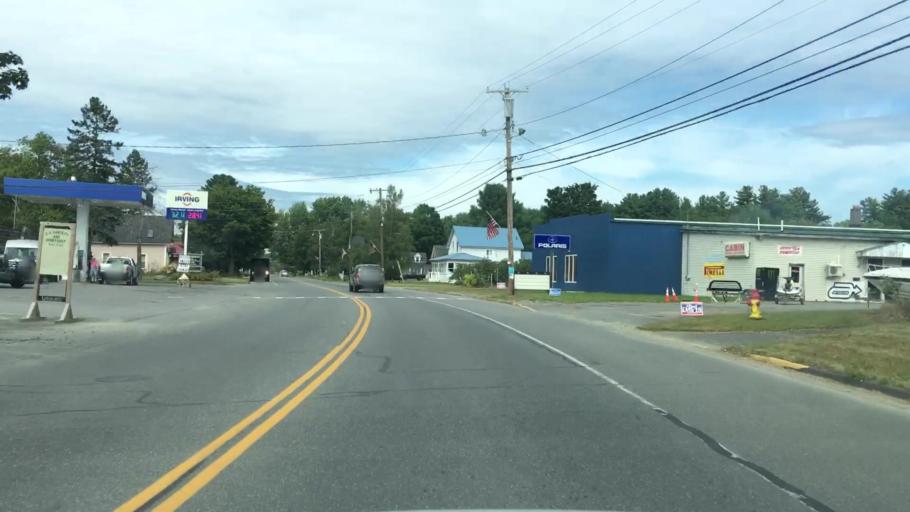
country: US
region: Maine
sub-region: Piscataquis County
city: Milo
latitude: 45.2609
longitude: -68.9883
